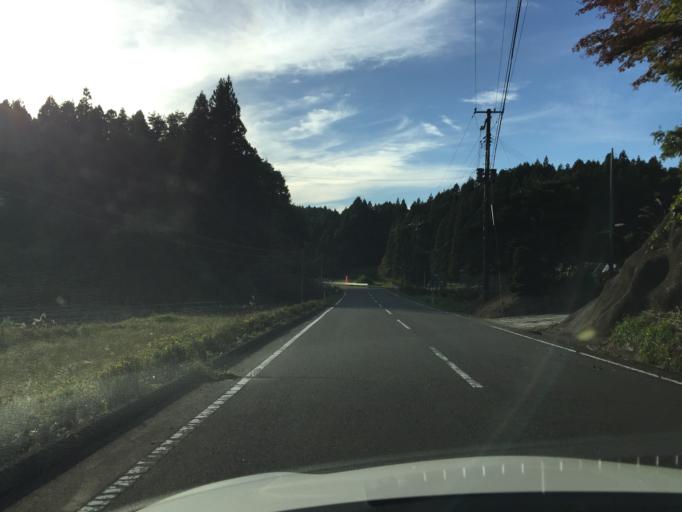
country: JP
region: Fukushima
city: Ishikawa
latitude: 37.2057
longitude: 140.5920
